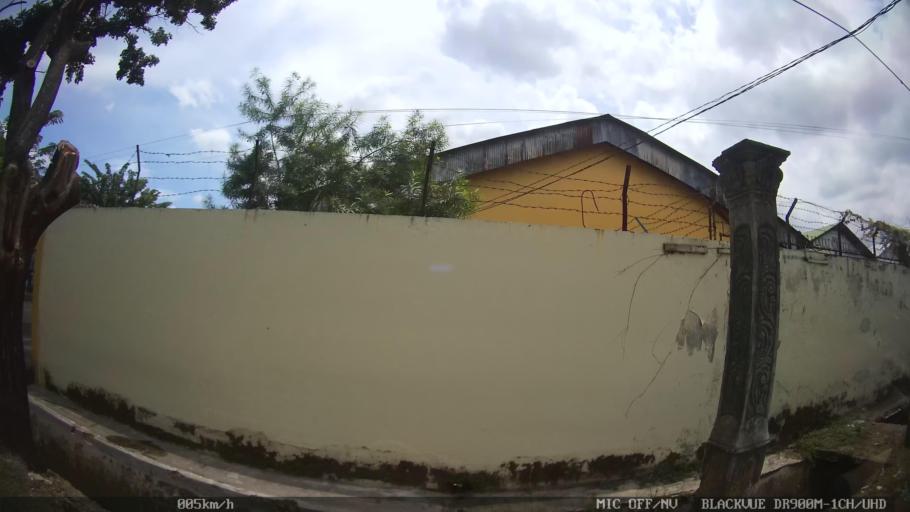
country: ID
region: North Sumatra
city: Medan
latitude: 3.6259
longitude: 98.6806
